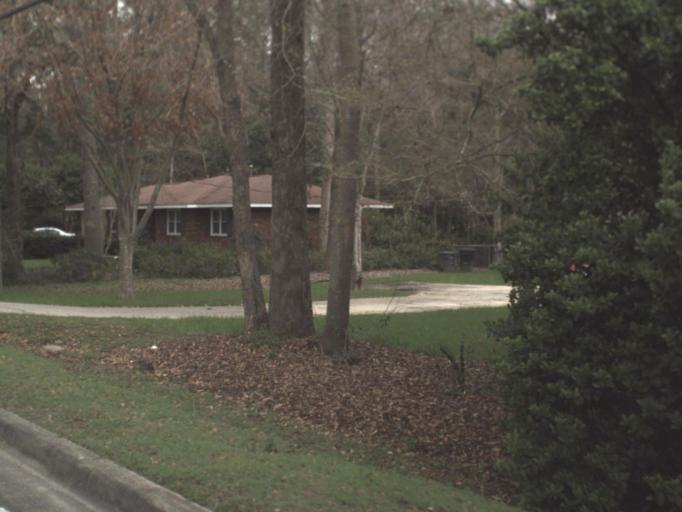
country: US
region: Florida
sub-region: Leon County
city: Tallahassee
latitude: 30.4818
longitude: -84.2772
